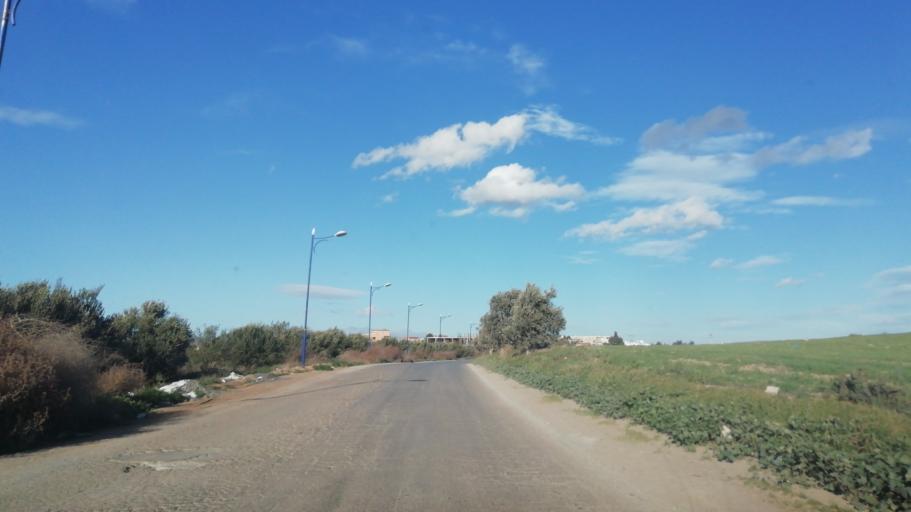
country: DZ
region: Oran
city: Sidi ech Chahmi
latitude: 35.6518
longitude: -0.5299
